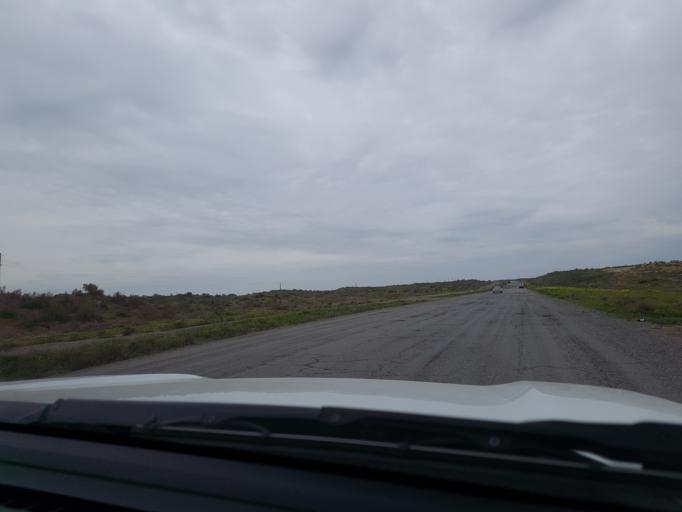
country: TM
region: Mary
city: Bayramaly
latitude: 37.9003
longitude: 62.6178
